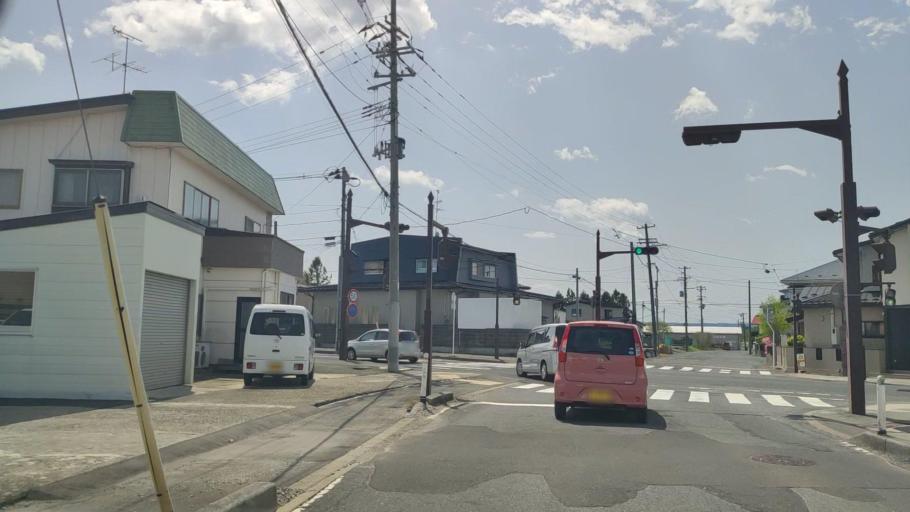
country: JP
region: Aomori
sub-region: Hachinohe Shi
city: Uchimaru
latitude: 40.5074
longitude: 141.4355
